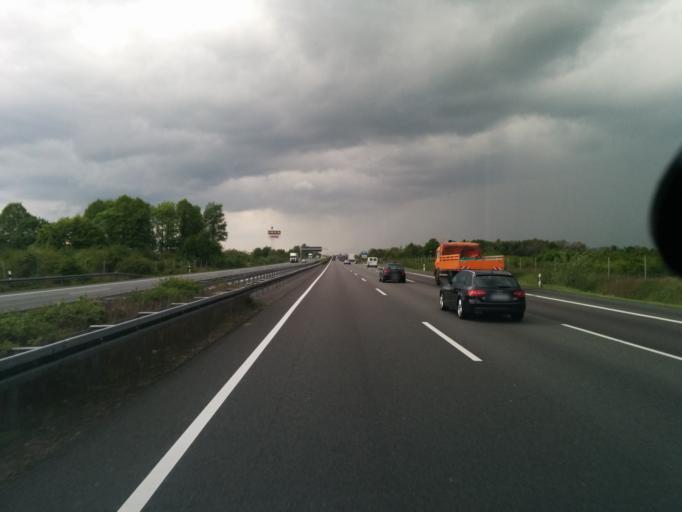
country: DE
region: Lower Saxony
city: Vordorf
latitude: 52.3188
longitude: 10.4991
